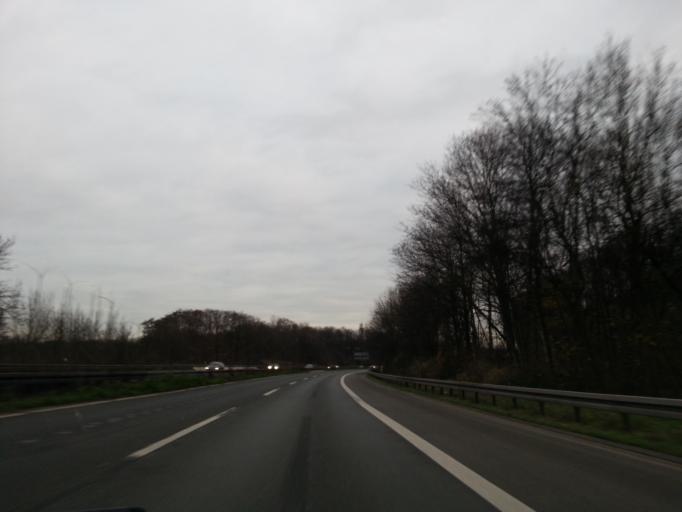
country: DE
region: North Rhine-Westphalia
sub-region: Regierungsbezirk Dusseldorf
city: Duisburg
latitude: 51.4406
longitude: 6.8043
